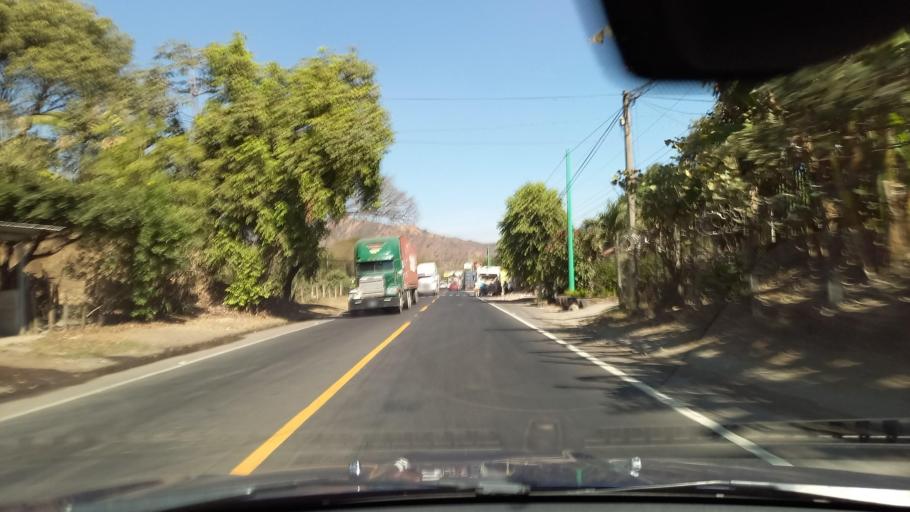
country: SV
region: Santa Ana
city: Santa Ana
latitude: 14.0018
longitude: -89.5417
